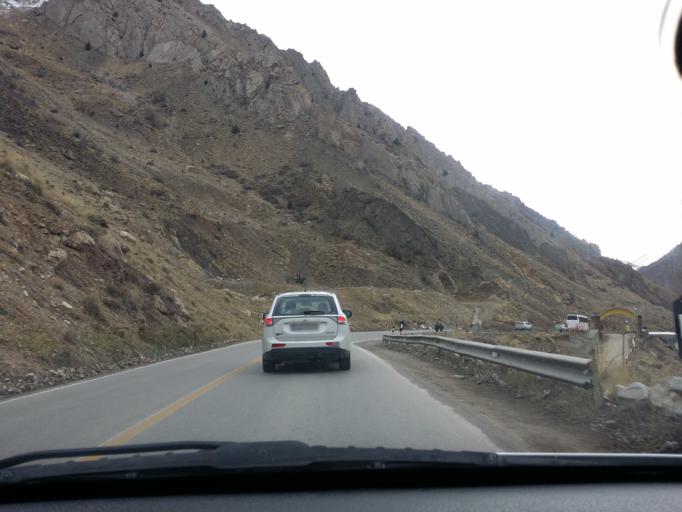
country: IR
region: Tehran
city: Tajrish
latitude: 36.0695
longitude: 51.3104
